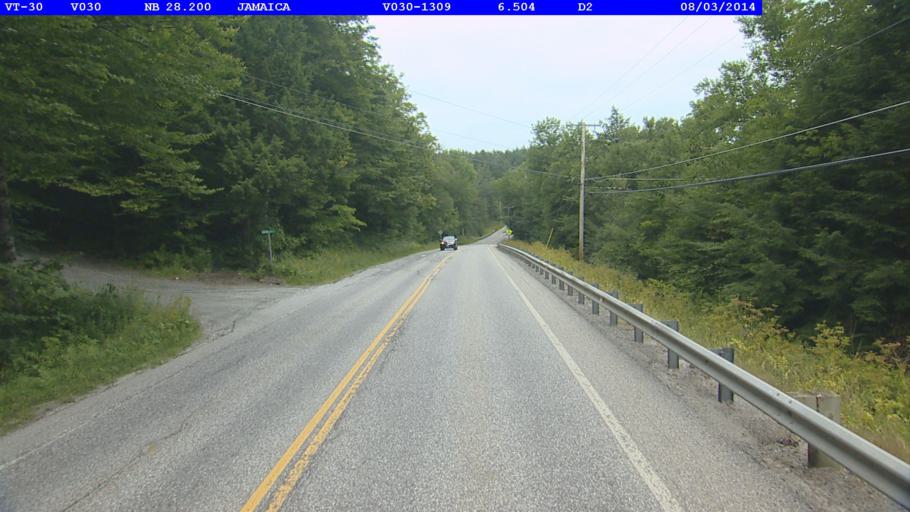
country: US
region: Vermont
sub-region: Windham County
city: Dover
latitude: 43.1242
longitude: -72.8117
